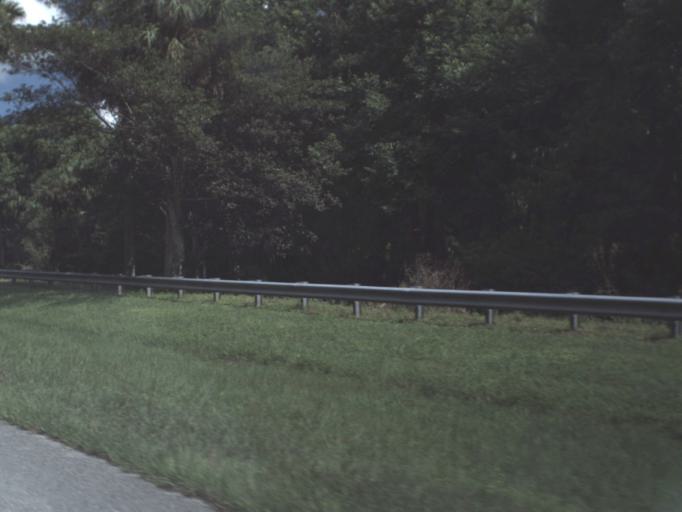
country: US
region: Florida
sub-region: Collier County
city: Immokalee
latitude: 26.2701
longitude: -81.3421
